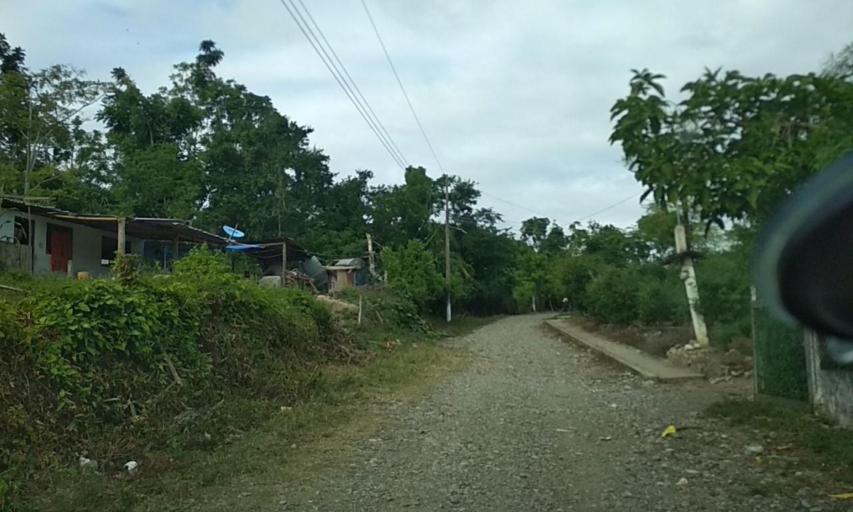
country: MX
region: Veracruz
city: Cazones de Herrera
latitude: 20.6482
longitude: -97.3382
